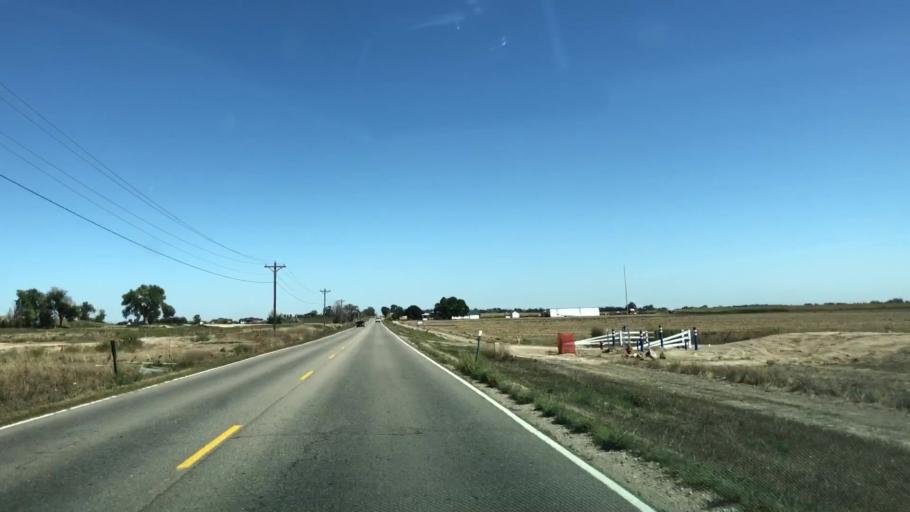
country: US
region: Colorado
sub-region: Weld County
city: Windsor
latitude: 40.5228
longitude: -104.9367
